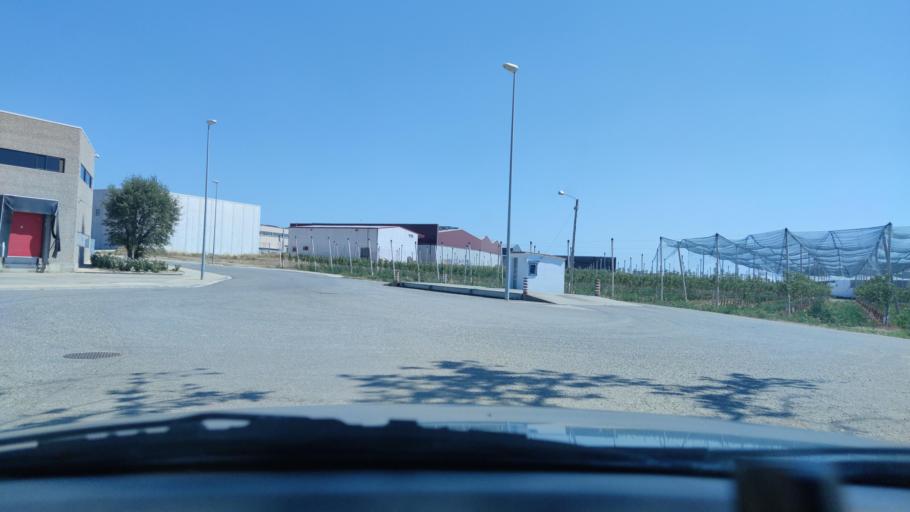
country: ES
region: Catalonia
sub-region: Provincia de Lleida
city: Torrefarrera
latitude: 41.6804
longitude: 0.6280
